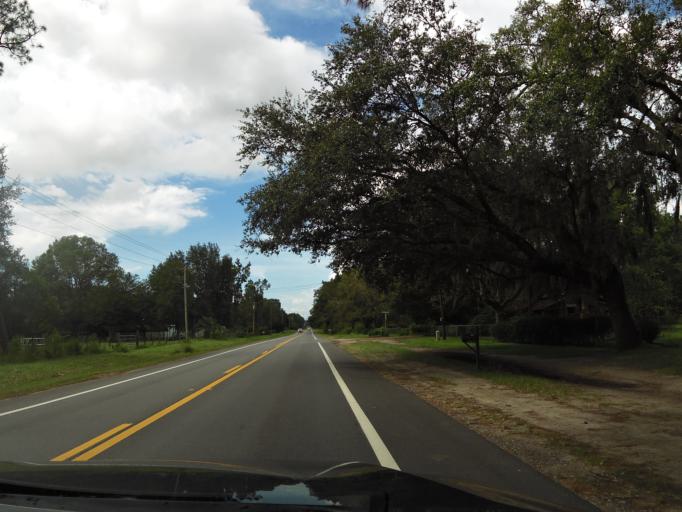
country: US
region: Florida
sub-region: Clay County
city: Middleburg
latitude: 30.1115
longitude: -81.9712
